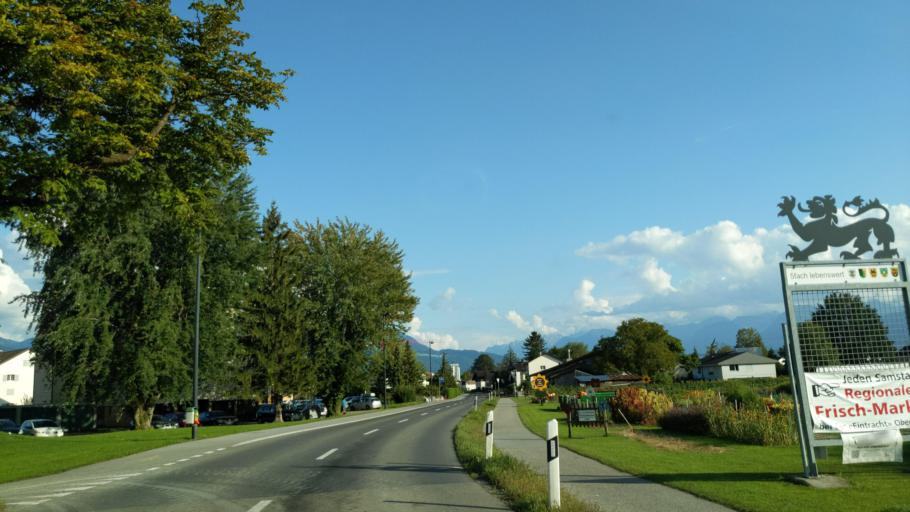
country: CH
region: Saint Gallen
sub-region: Wahlkreis Rheintal
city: Oberriet
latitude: 47.3284
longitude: 9.5628
